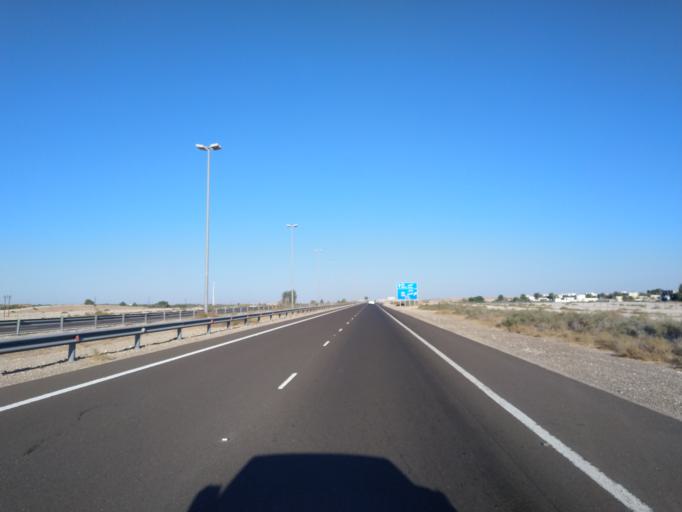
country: OM
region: Al Buraimi
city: Al Buraymi
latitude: 24.5241
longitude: 55.5430
